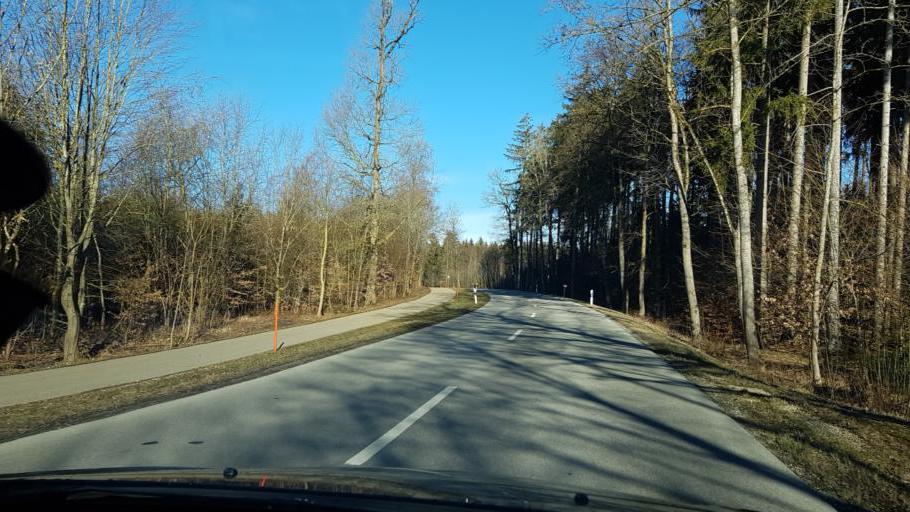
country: DE
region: Bavaria
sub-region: Upper Bavaria
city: Oberschweinbach
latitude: 48.2311
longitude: 11.1686
